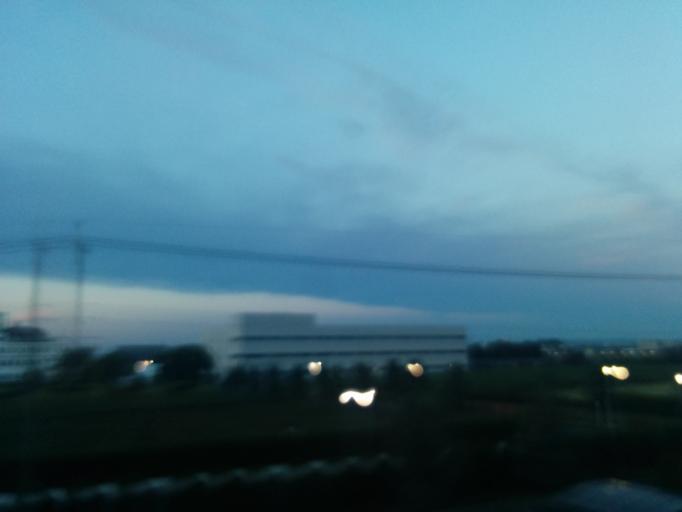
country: JP
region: Aichi
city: Inazawa
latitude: 35.2233
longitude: 136.8314
